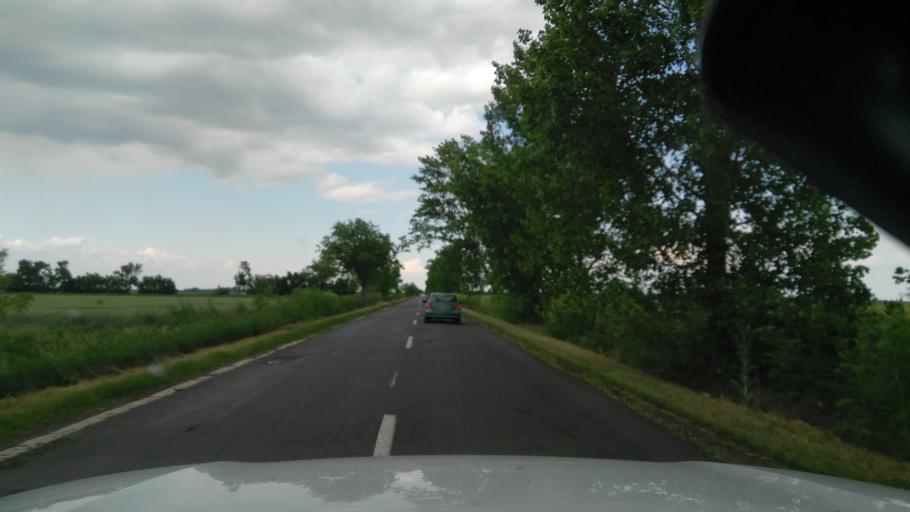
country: HU
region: Bekes
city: Magyarbanhegyes
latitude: 46.4610
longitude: 21.0059
